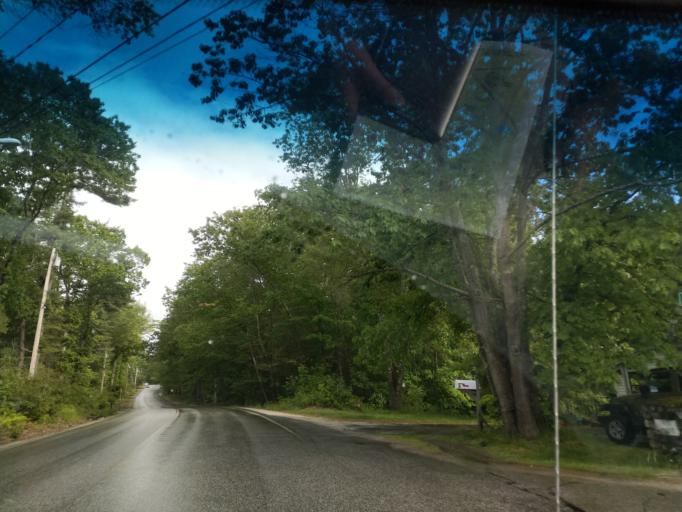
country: US
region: Maine
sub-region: Cumberland County
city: South Windham
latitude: 43.7890
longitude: -70.3521
